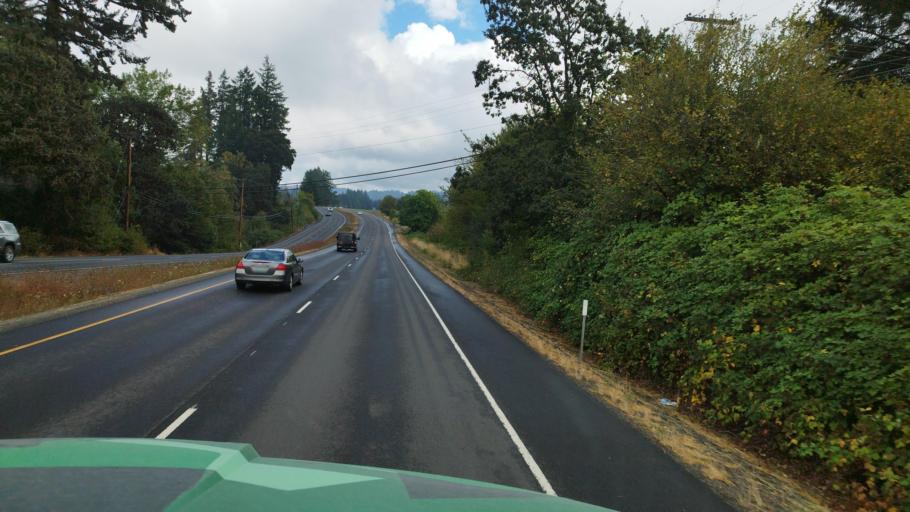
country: US
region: Oregon
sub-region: Yamhill County
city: Lafayette
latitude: 45.2414
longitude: -123.1360
